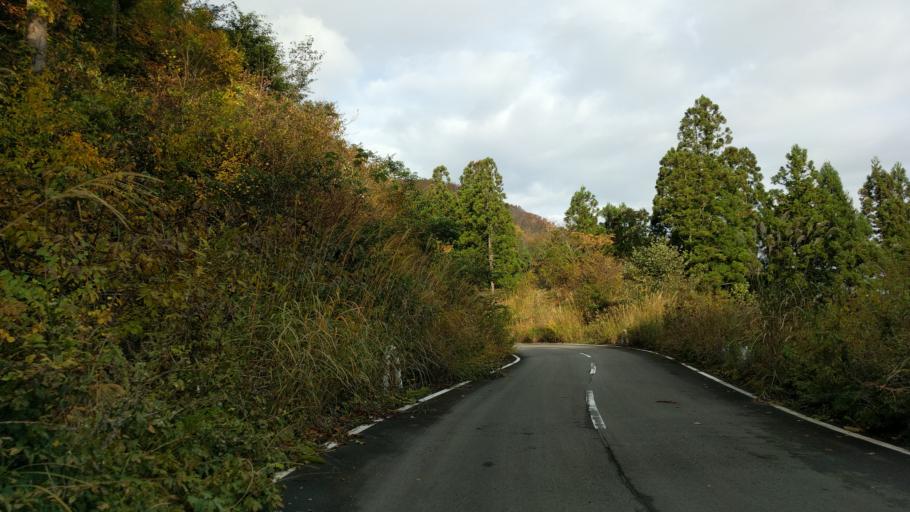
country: JP
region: Fukushima
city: Kitakata
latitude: 37.3797
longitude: 139.7251
